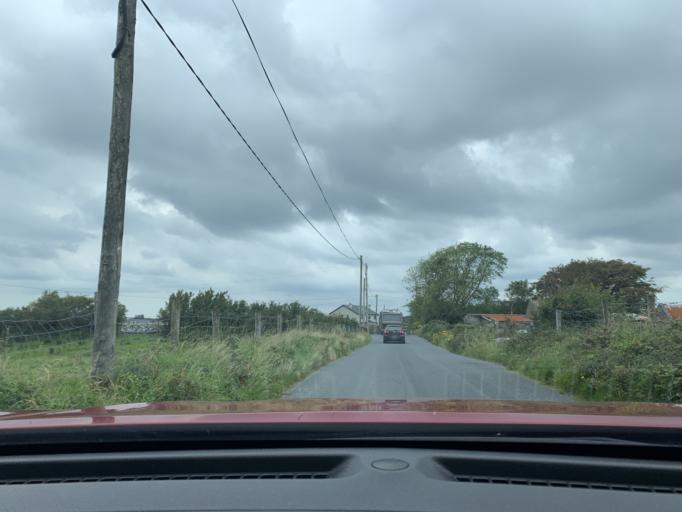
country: IE
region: Connaught
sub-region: County Galway
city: Bearna
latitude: 53.2761
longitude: -9.1179
